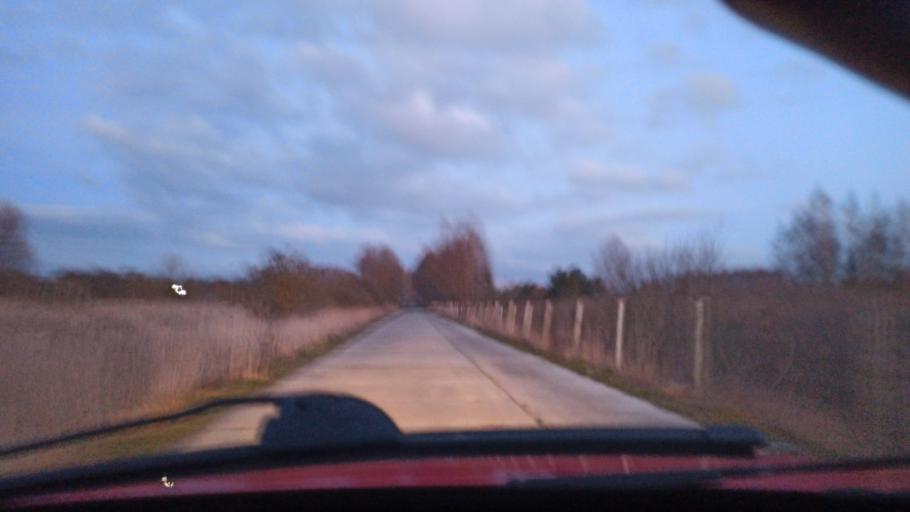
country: PL
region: Warmian-Masurian Voivodeship
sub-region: Powiat elblaski
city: Elblag
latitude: 54.1372
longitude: 19.4082
